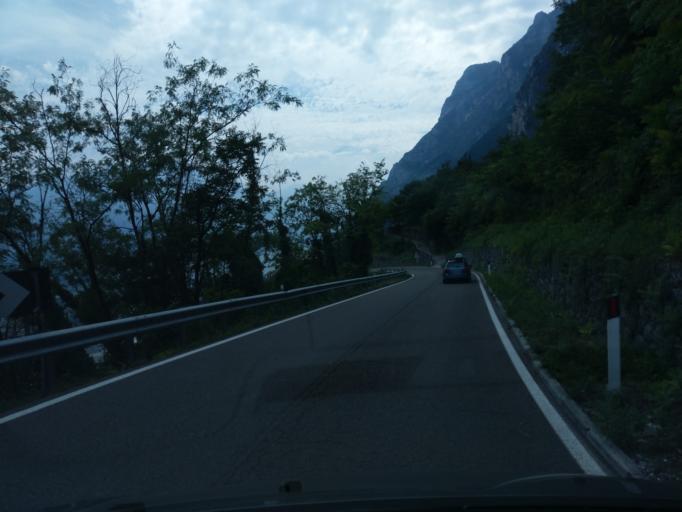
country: IT
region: Trentino-Alto Adige
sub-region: Provincia di Trento
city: Tenno
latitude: 45.9083
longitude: 10.8329
